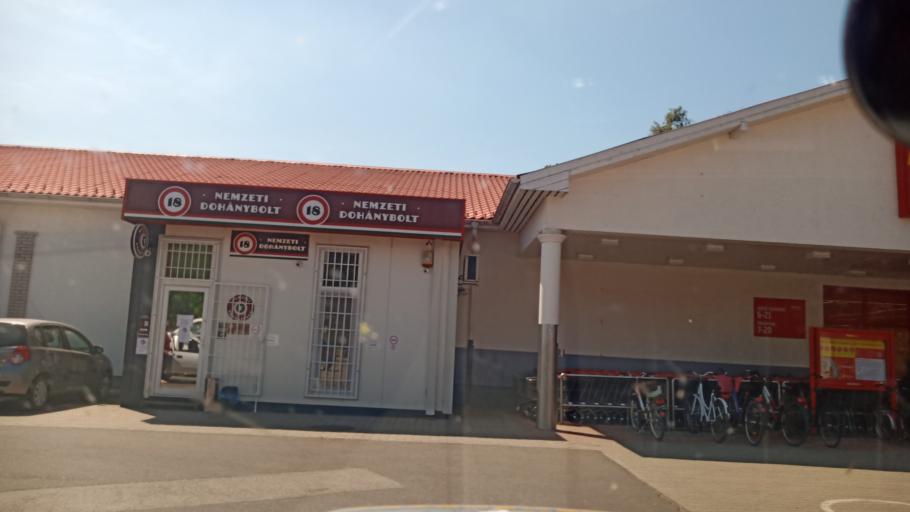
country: HU
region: Bekes
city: Oroshaza
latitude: 46.5566
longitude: 20.6632
